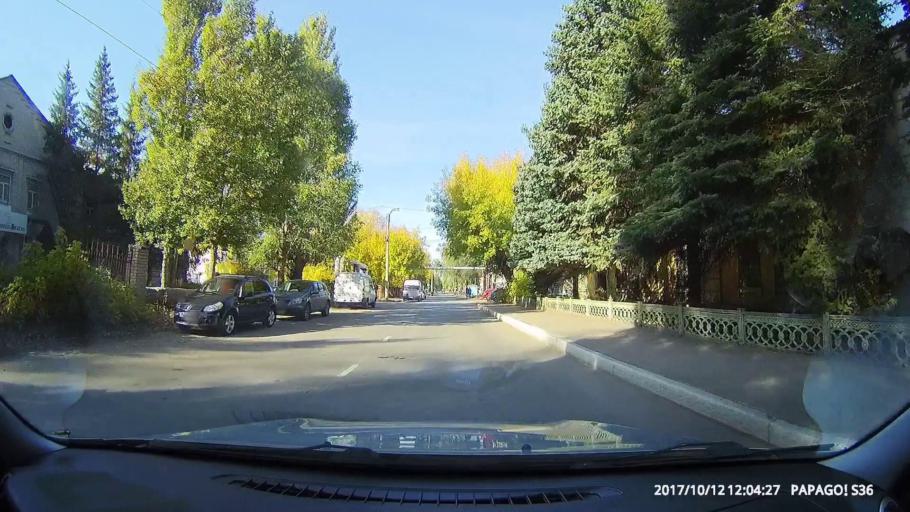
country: RU
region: Samara
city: Chapayevsk
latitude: 52.9780
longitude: 49.7162
